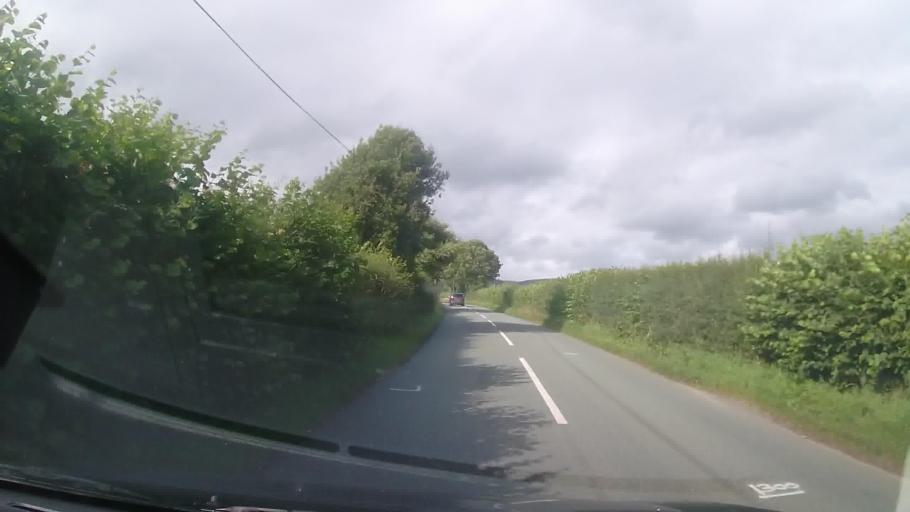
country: GB
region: England
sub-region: Shropshire
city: Norbury
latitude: 52.5171
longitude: -2.9487
